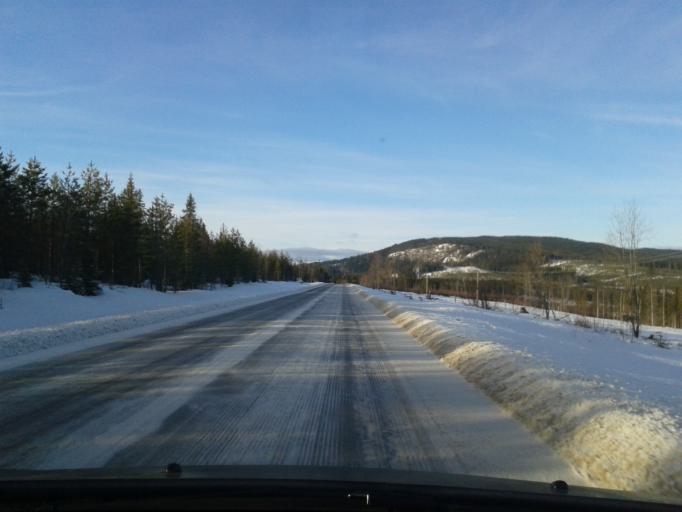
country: SE
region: Vaesterbotten
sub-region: Asele Kommun
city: Asele
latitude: 63.7744
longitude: 17.6750
